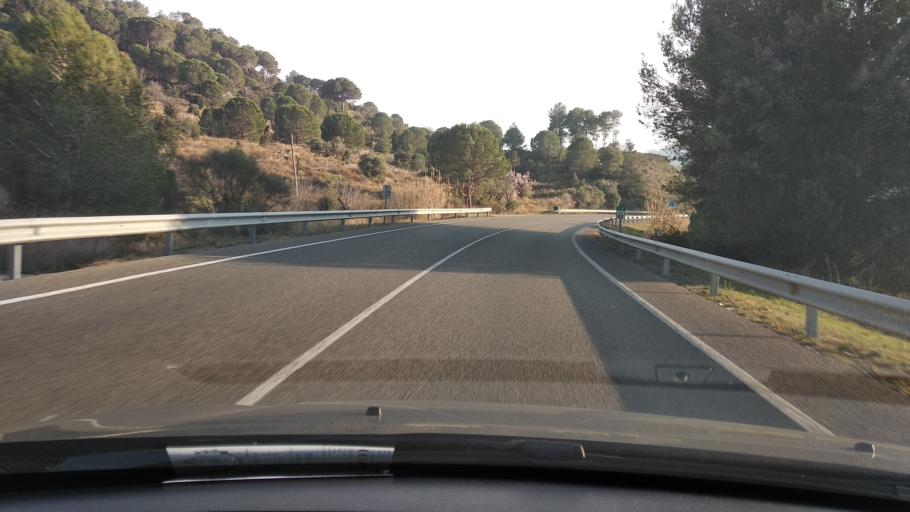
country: ES
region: Catalonia
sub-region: Provincia de Tarragona
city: Alforja
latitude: 41.1977
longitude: 0.9982
